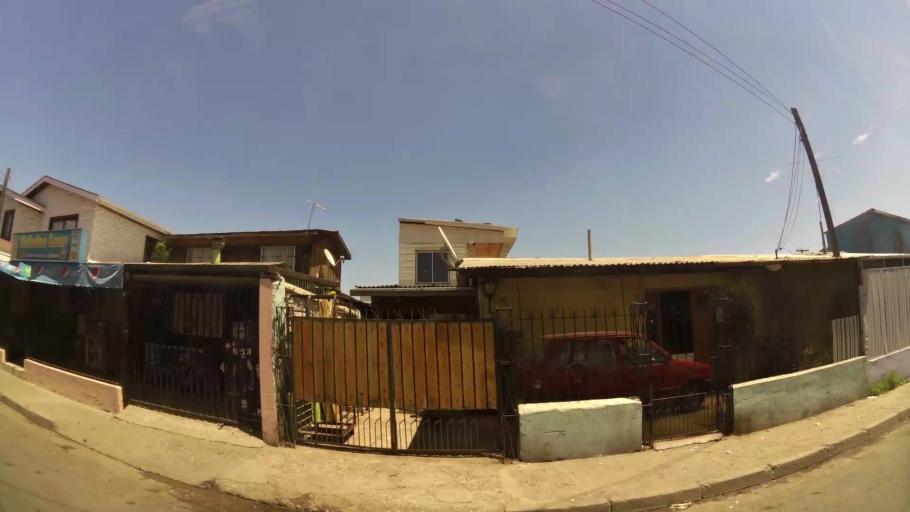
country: CL
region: Santiago Metropolitan
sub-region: Provincia de Santiago
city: La Pintana
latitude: -33.5497
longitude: -70.6462
